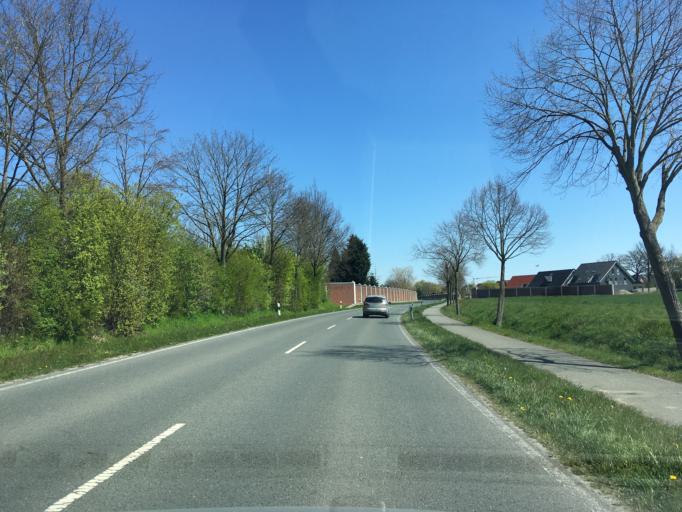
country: DE
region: North Rhine-Westphalia
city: Stadtlohn
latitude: 51.9843
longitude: 6.9363
